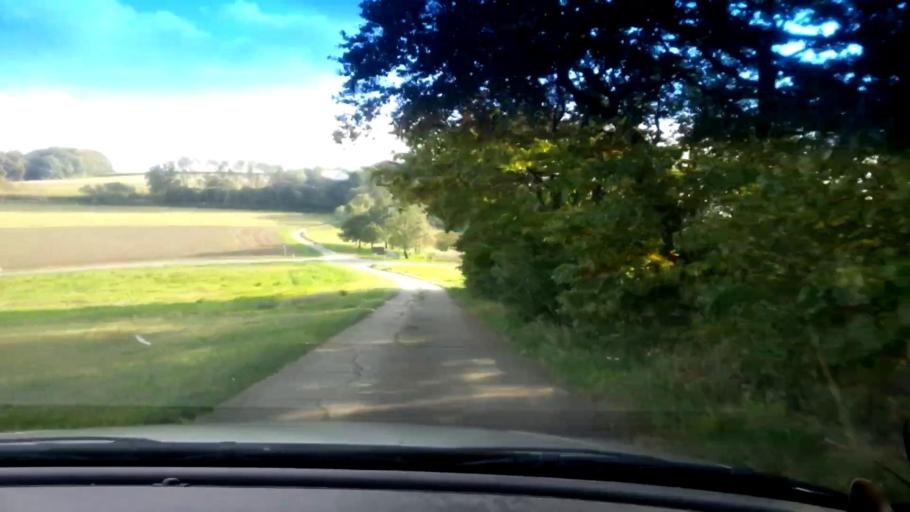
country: DE
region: Bavaria
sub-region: Upper Franconia
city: Schesslitz
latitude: 50.0113
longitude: 11.0354
